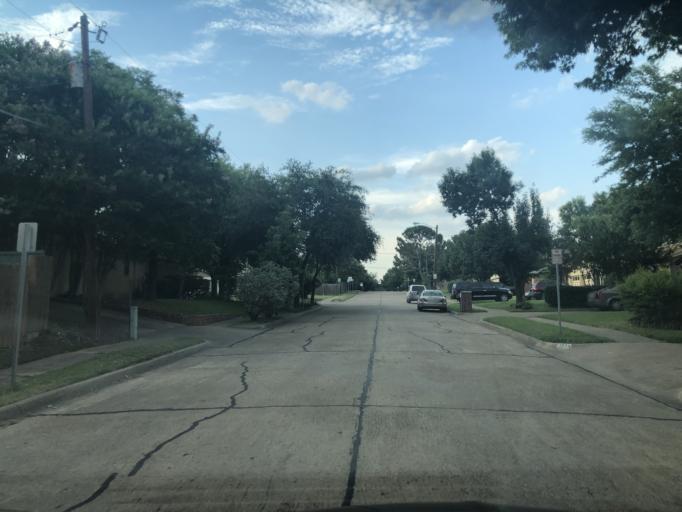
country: US
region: Texas
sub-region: Dallas County
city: Irving
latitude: 32.7926
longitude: -96.9507
